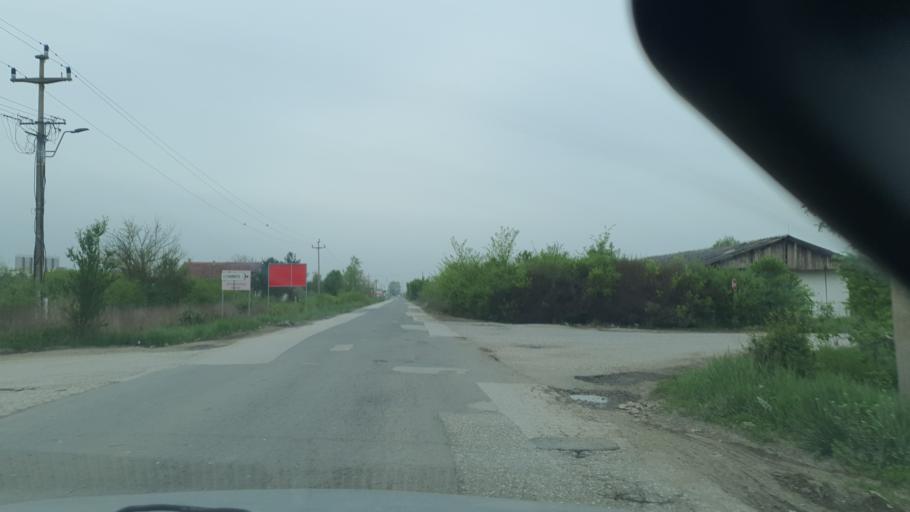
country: RS
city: Simanovci
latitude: 44.8830
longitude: 20.1326
